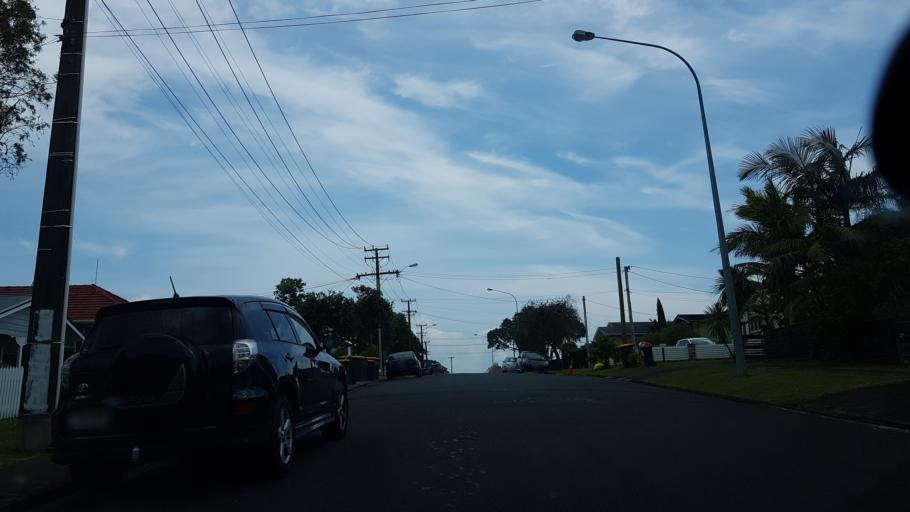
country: NZ
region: Auckland
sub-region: Auckland
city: North Shore
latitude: -36.8060
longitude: 174.7841
